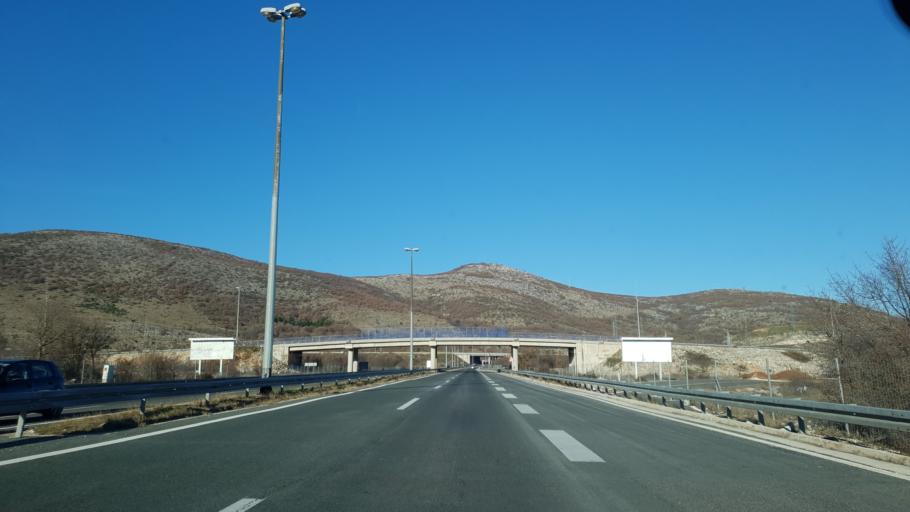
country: HR
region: Splitsko-Dalmatinska
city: Dugopolje
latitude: 43.5960
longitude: 16.5762
